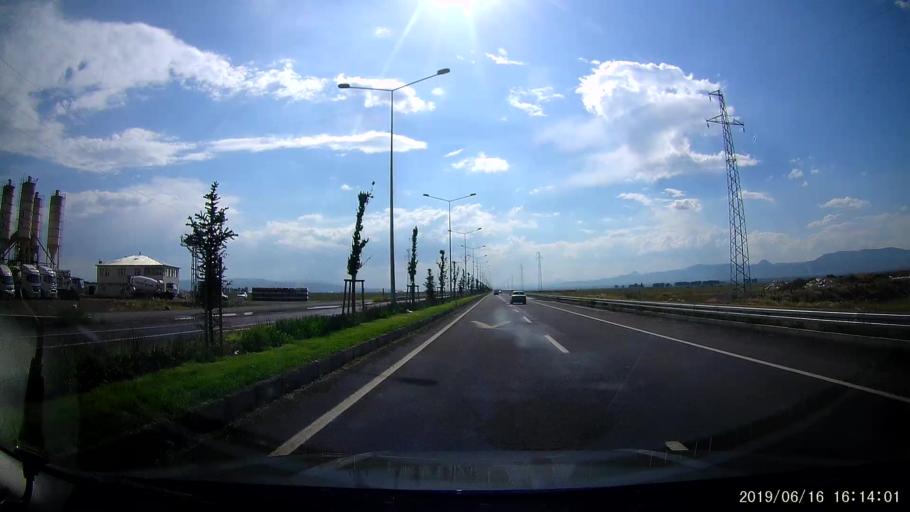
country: TR
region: Erzurum
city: Erzurum
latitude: 39.9602
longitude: 41.2595
